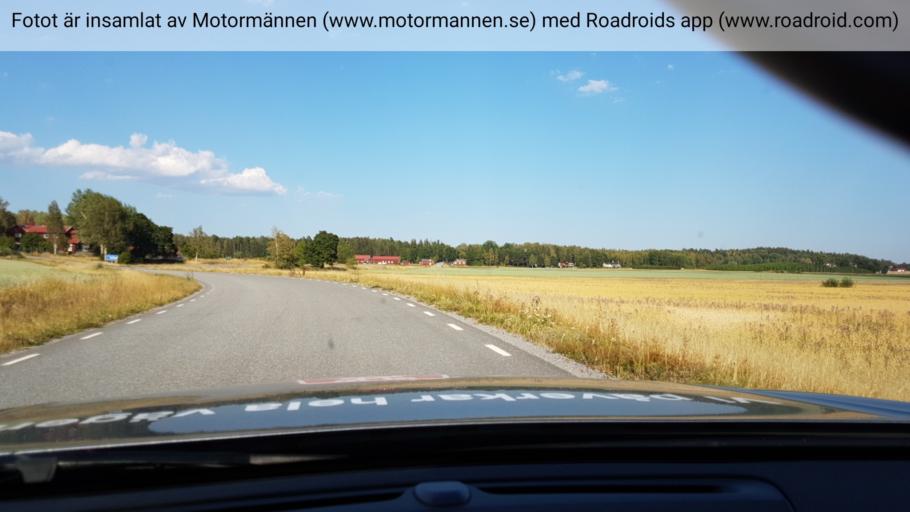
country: SE
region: Uppsala
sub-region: Enkopings Kommun
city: Enkoping
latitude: 59.7116
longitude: 17.0639
